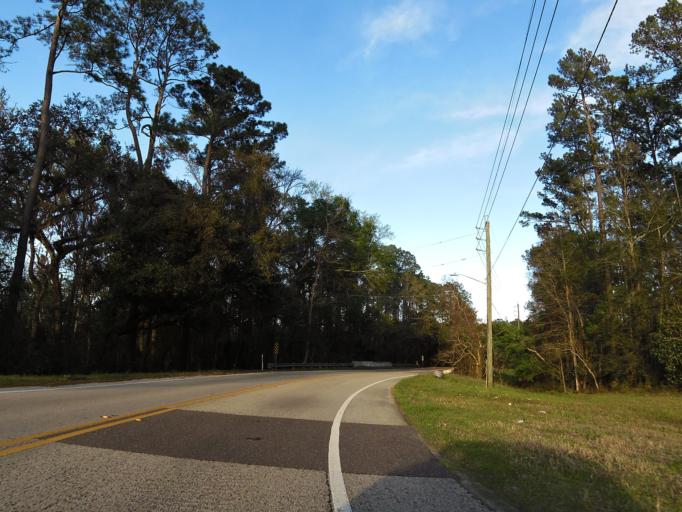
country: US
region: Florida
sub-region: Duval County
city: Jacksonville
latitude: 30.4667
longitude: -81.6687
